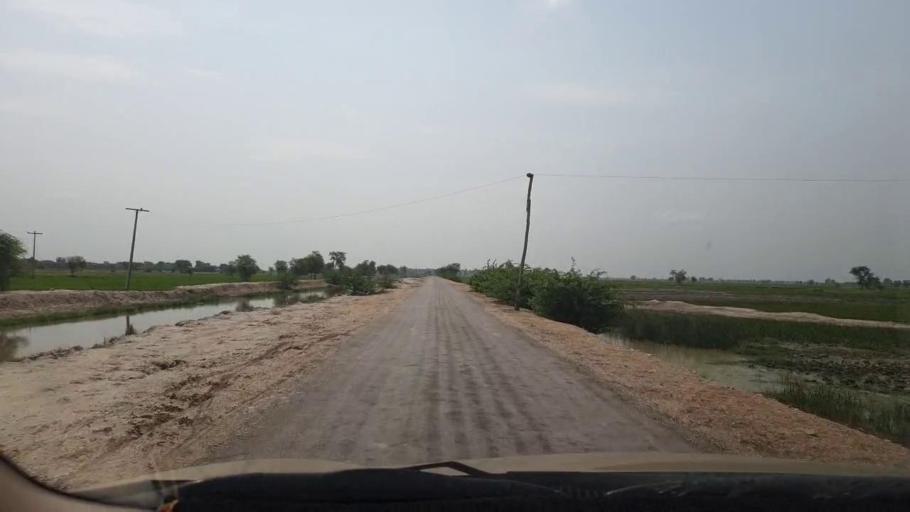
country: PK
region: Sindh
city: Goth Garelo
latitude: 27.5157
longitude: 68.1051
